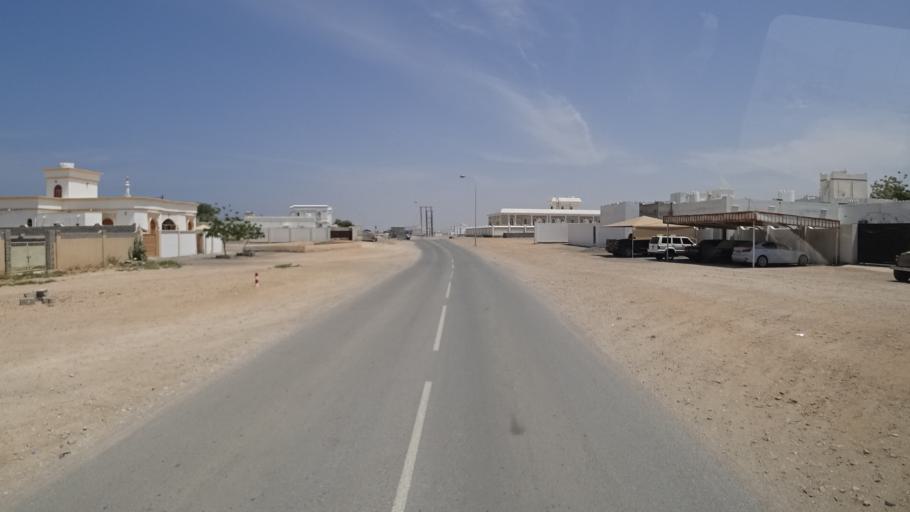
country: OM
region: Ash Sharqiyah
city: Sur
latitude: 22.6117
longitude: 59.4656
